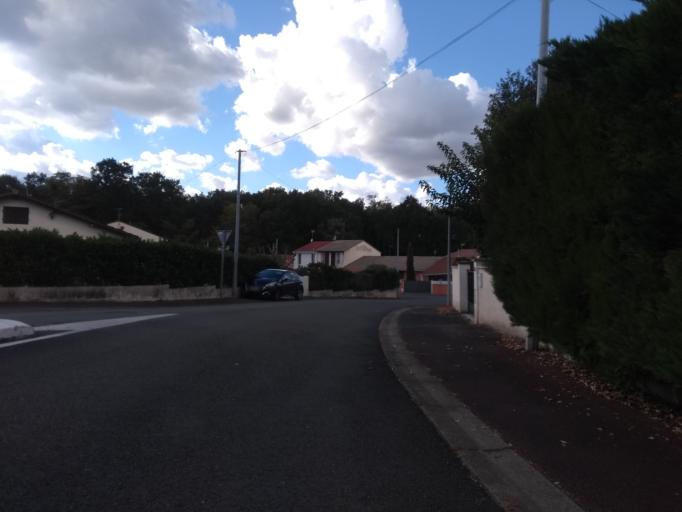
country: FR
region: Aquitaine
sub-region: Departement de la Gironde
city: Canejan
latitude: 44.7569
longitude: -0.6419
